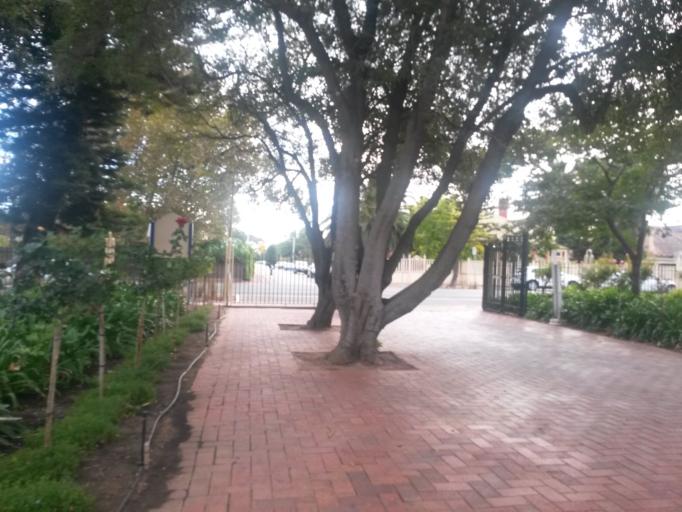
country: AU
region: South Australia
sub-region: Adelaide
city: Glenelg
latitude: -34.9828
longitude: 138.5182
